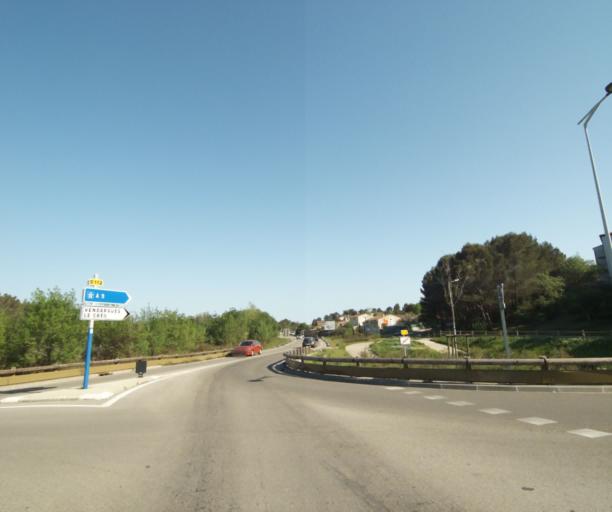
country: FR
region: Languedoc-Roussillon
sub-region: Departement de l'Herault
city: Jacou
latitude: 43.6622
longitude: 3.9258
